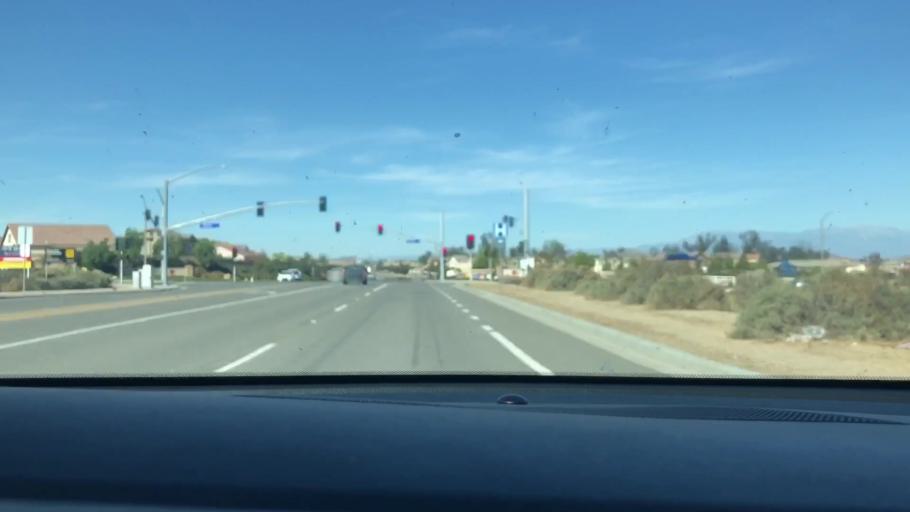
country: US
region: California
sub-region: Riverside County
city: Murrieta Hot Springs
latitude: 33.6115
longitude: -117.1625
